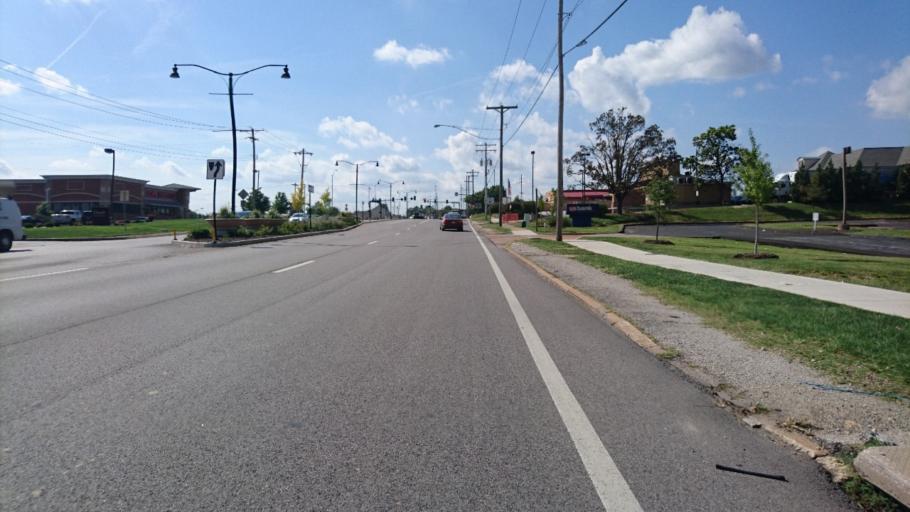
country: US
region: Missouri
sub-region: Saint Louis County
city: Ellisville
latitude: 38.5928
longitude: -90.5838
